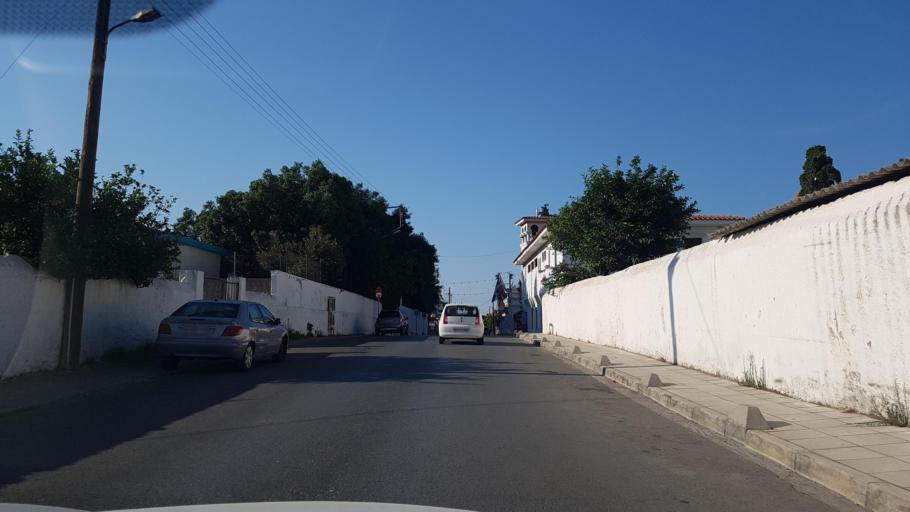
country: GR
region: Crete
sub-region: Nomos Chanias
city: Chania
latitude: 35.5068
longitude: 24.0197
